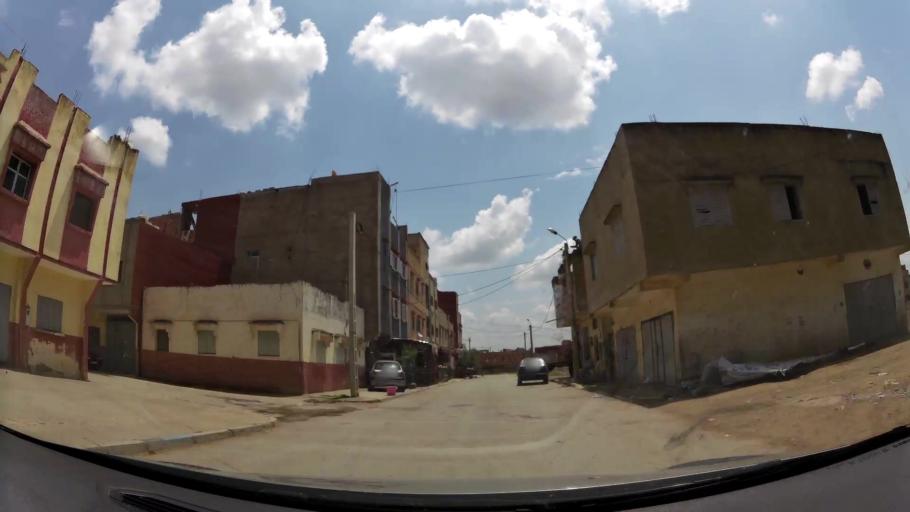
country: MA
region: Rabat-Sale-Zemmour-Zaer
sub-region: Khemisset
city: Tiflet
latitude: 34.0007
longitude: -6.5313
